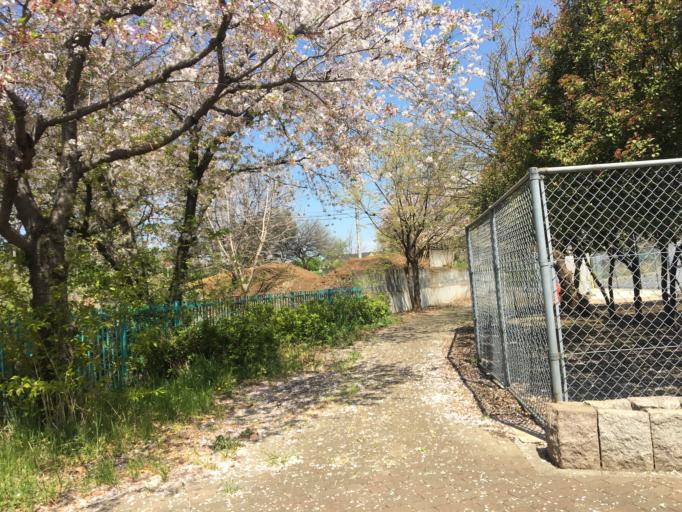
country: JP
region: Saitama
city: Shiki
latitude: 35.8263
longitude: 139.5514
